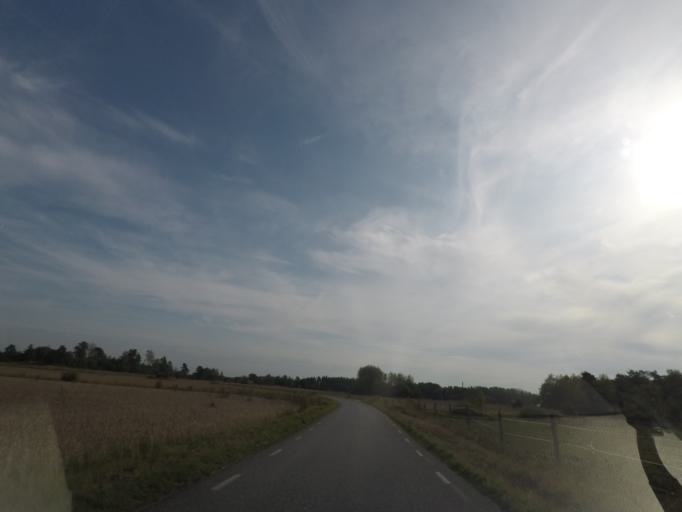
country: SE
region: Vaestmanland
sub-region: Kungsors Kommun
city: Kungsoer
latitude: 59.5263
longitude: 16.1429
